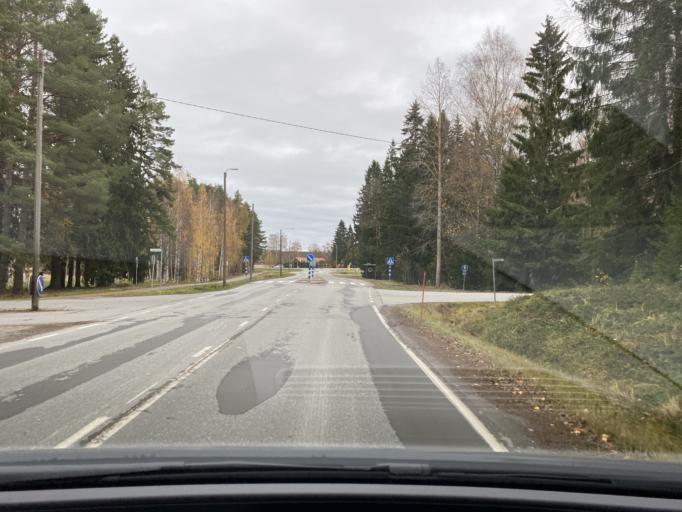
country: FI
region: Satakunta
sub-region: Pori
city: Luvia
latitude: 61.3660
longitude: 21.6442
